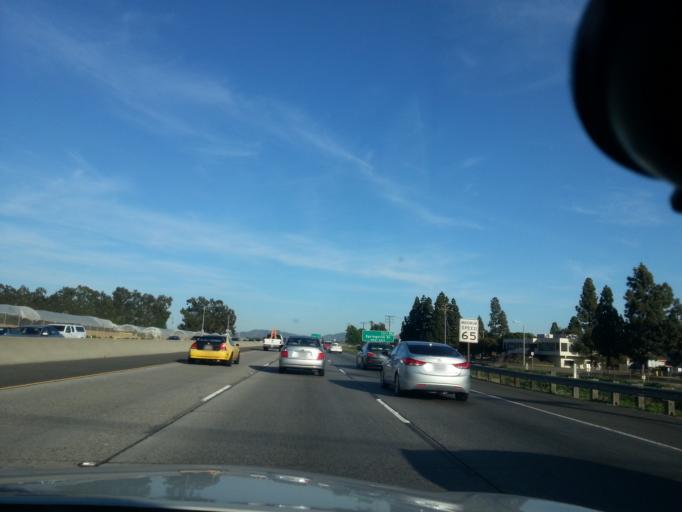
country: US
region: California
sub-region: Ventura County
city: Camarillo
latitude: 34.2212
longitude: -119.0961
